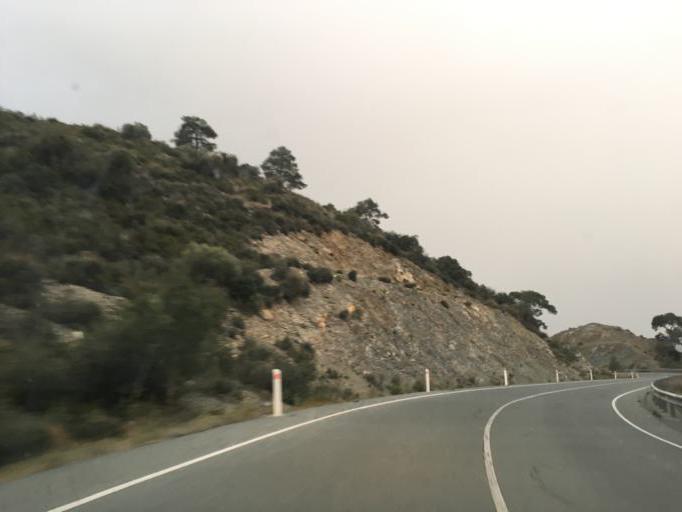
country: CY
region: Limassol
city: Parekklisha
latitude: 34.7970
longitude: 33.1559
